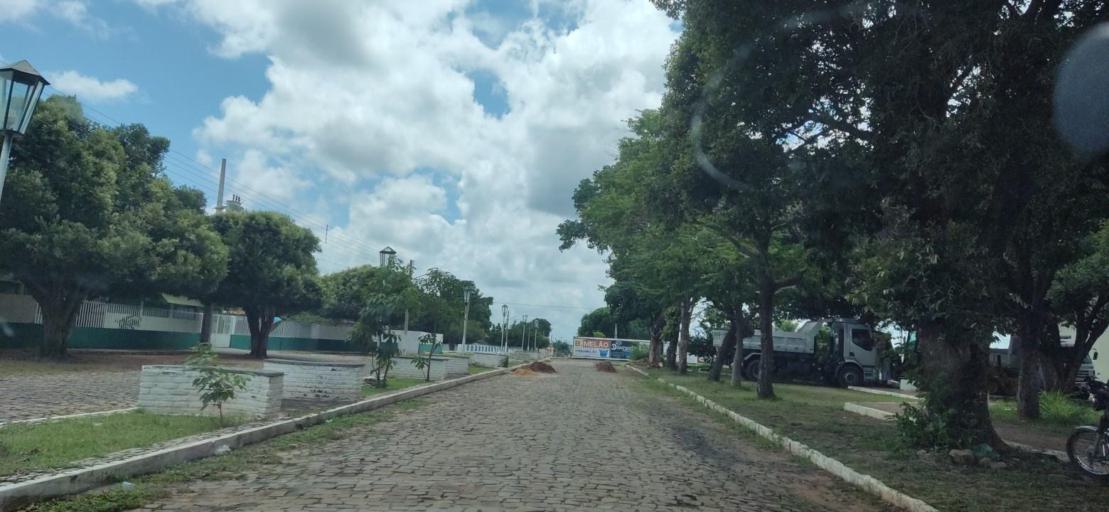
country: BR
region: Piaui
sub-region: Valenca Do Piaui
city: Valenca do Piaui
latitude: -6.4016
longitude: -41.7357
